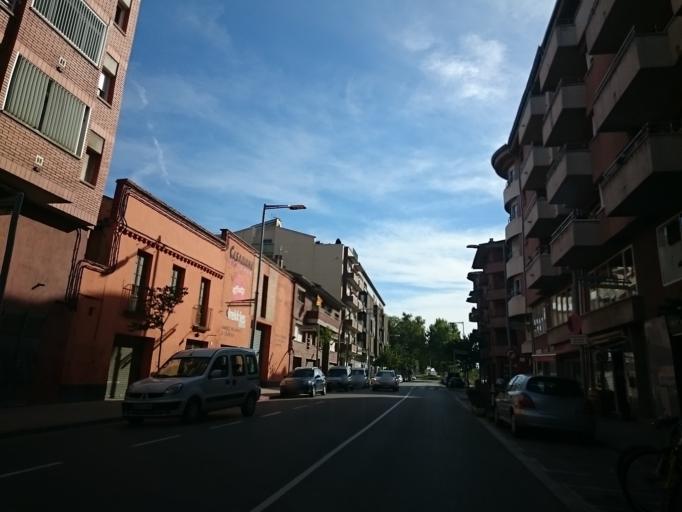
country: ES
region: Catalonia
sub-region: Provincia de Barcelona
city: Vic
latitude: 41.9201
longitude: 2.2523
